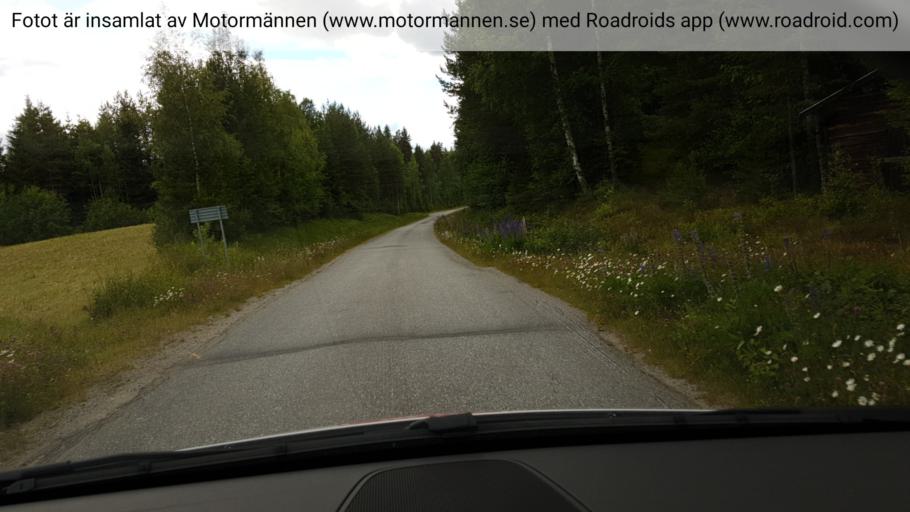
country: SE
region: Vaesterbotten
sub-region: Dorotea Kommun
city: Dorotea
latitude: 63.9119
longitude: 16.2877
